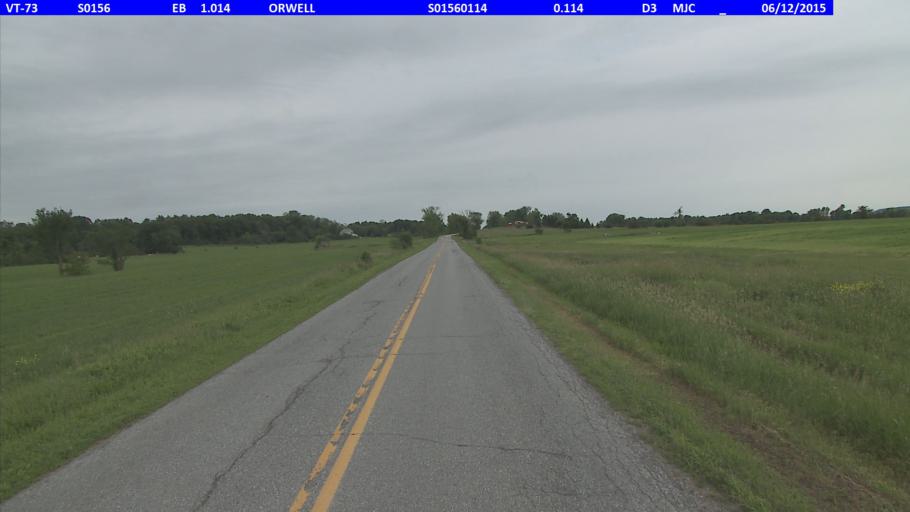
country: US
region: New York
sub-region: Essex County
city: Ticonderoga
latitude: 43.8426
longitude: -73.3619
